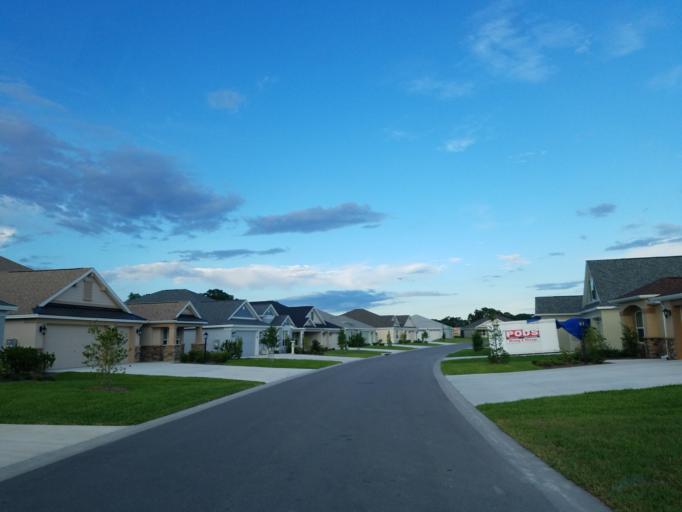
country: US
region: Florida
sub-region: Sumter County
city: Wildwood
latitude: 28.7953
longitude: -82.0227
